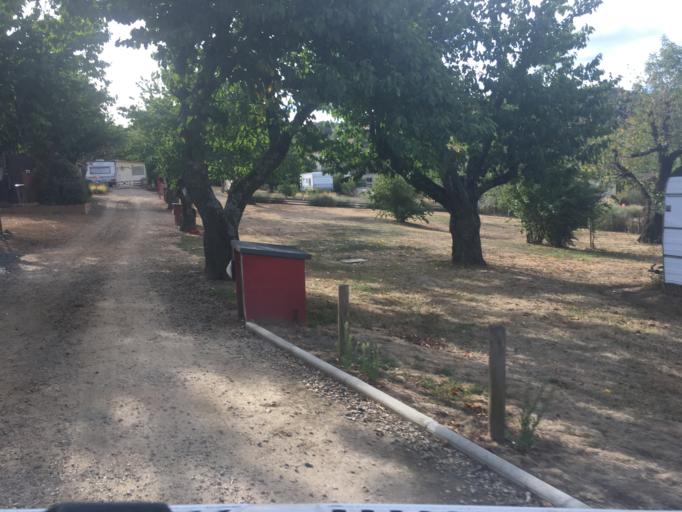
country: FR
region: Rhone-Alpes
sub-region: Departement du Rhone
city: Sourcieux-les-Mines
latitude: 45.8171
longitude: 4.6278
